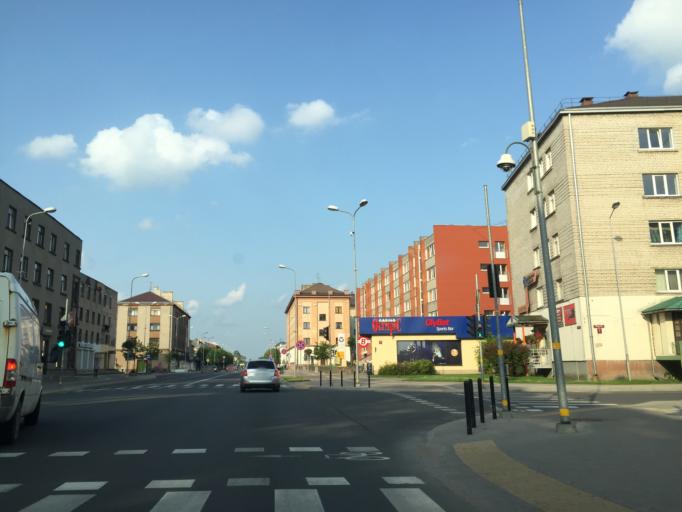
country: LV
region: Jelgava
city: Jelgava
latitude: 56.6504
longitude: 23.7165
